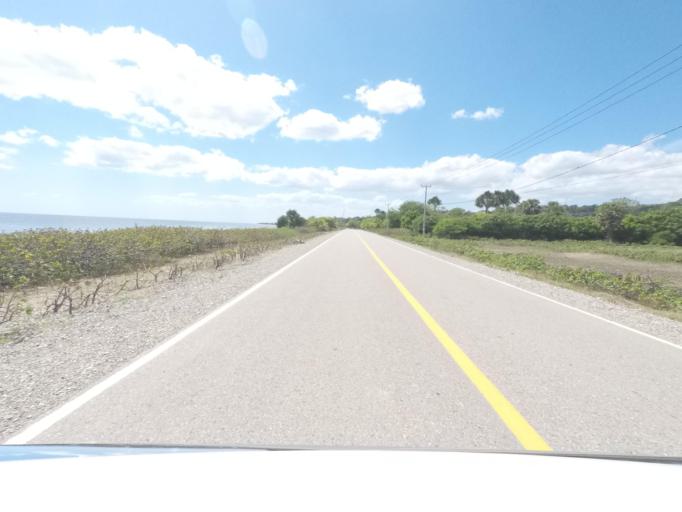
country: TL
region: Baucau
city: Baucau
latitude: -8.4517
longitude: 126.6360
